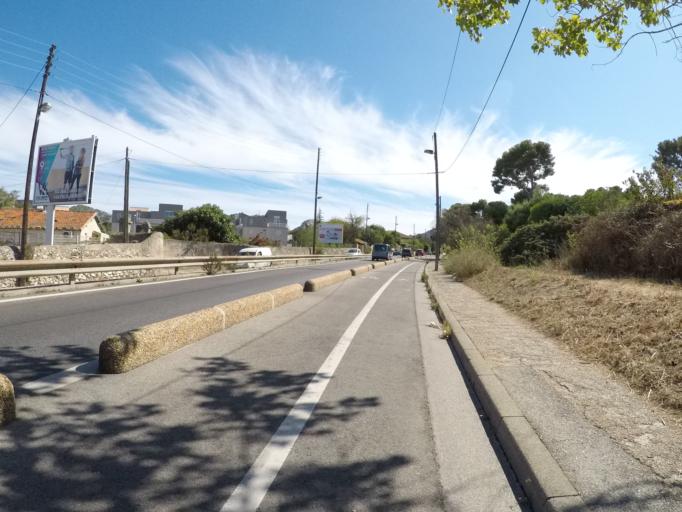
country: FR
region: Provence-Alpes-Cote d'Azur
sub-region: Departement des Bouches-du-Rhone
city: Marseille 09
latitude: 43.2375
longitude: 5.3986
